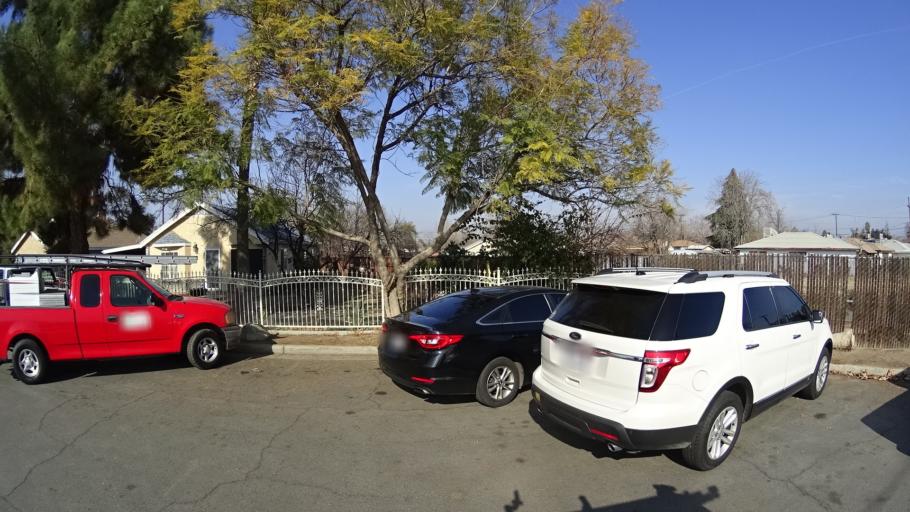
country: US
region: California
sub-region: Kern County
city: Bakersfield
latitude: 35.3627
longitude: -119.0090
